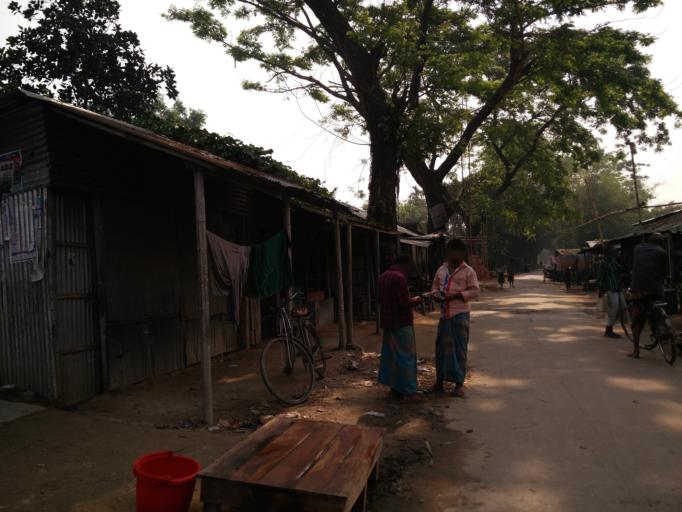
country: BD
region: Dhaka
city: Muktagacha
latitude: 24.9103
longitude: 90.1594
